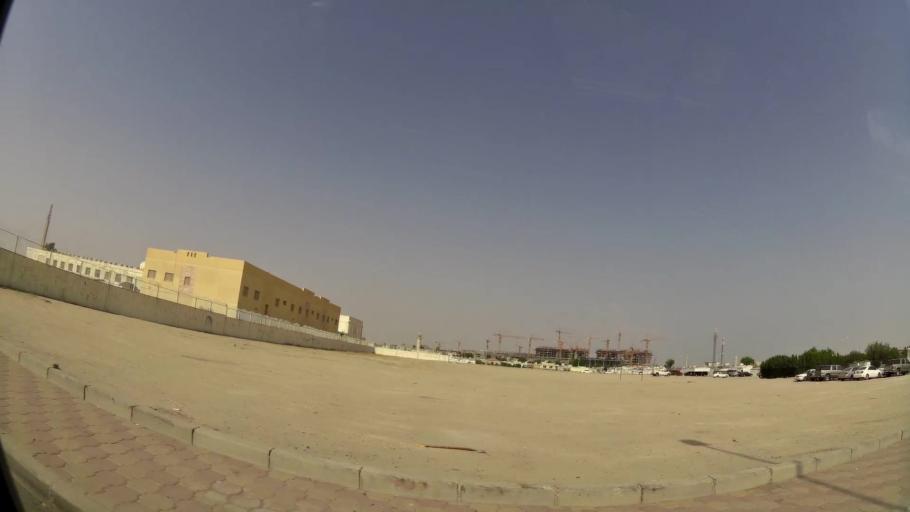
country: KW
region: Muhafazat al Jahra'
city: Al Jahra'
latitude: 29.3300
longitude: 47.6772
